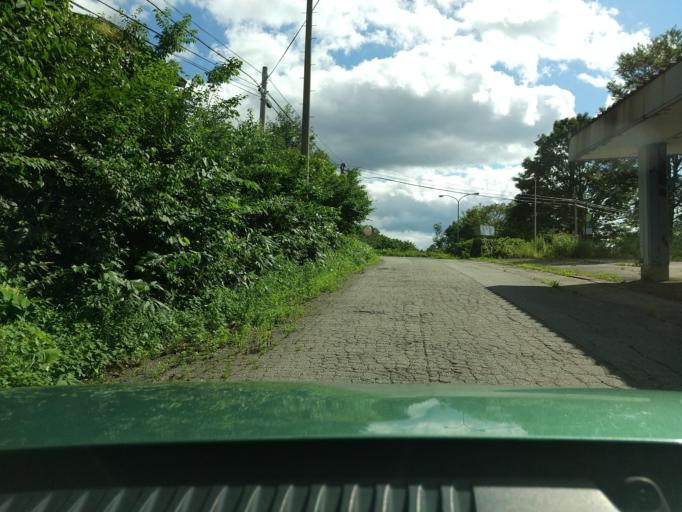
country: JP
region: Iwate
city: Shizukuishi
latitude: 39.7793
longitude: 140.7616
